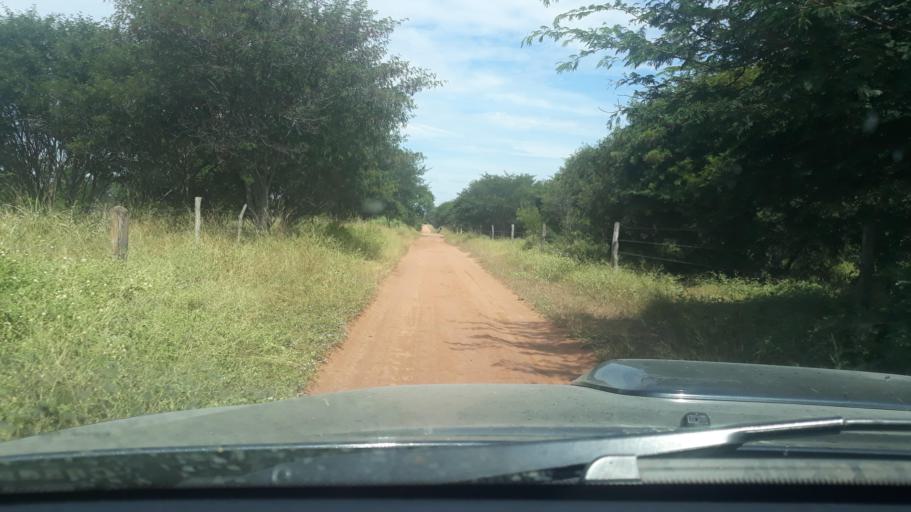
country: BR
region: Bahia
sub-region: Riacho De Santana
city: Riacho de Santana
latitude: -13.8588
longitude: -43.0659
